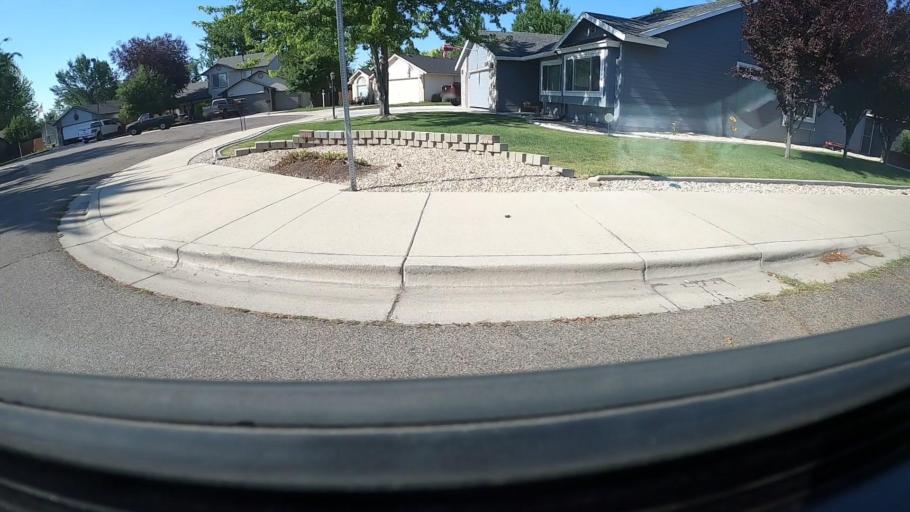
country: US
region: Idaho
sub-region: Ada County
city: Meridian
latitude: 43.6242
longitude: -116.3659
